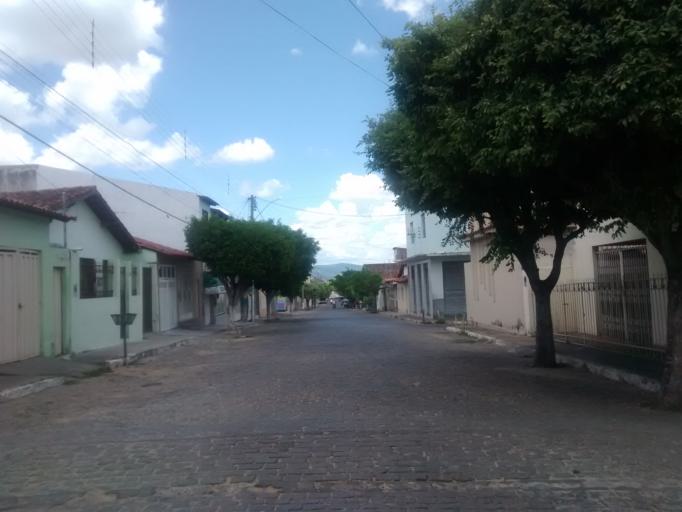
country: BR
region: Bahia
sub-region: Brumado
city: Brumado
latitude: -14.2074
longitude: -41.6744
